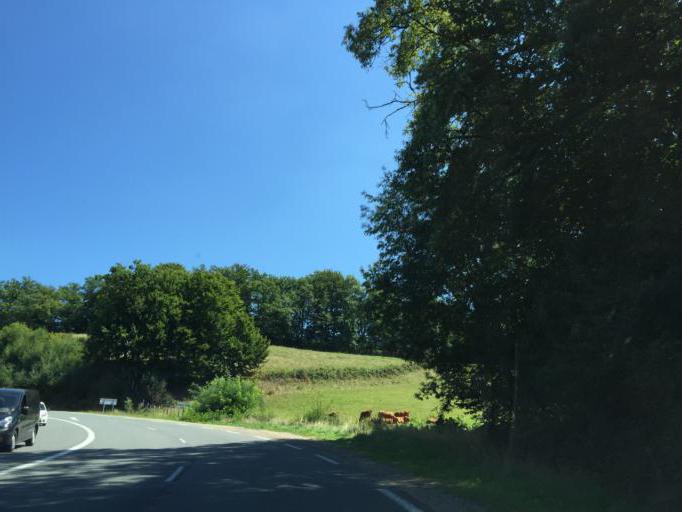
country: FR
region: Midi-Pyrenees
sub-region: Departement de l'Aveyron
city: Espalion
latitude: 44.5571
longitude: 2.7827
